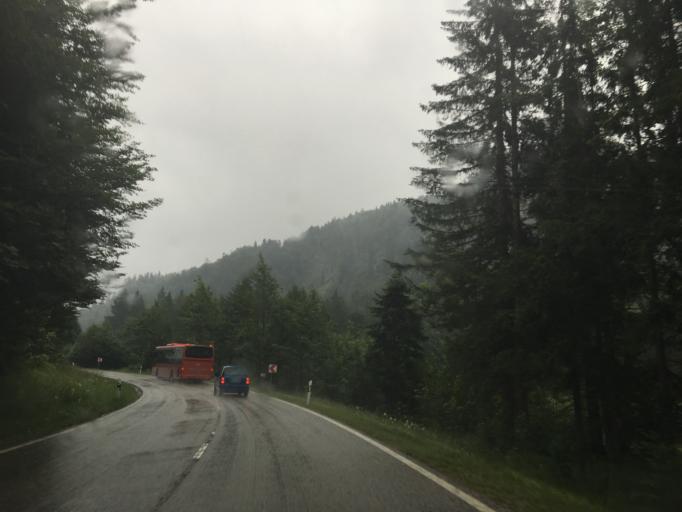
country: DE
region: Bavaria
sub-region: Upper Bavaria
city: Reit im Winkl
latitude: 47.6887
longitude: 12.4868
